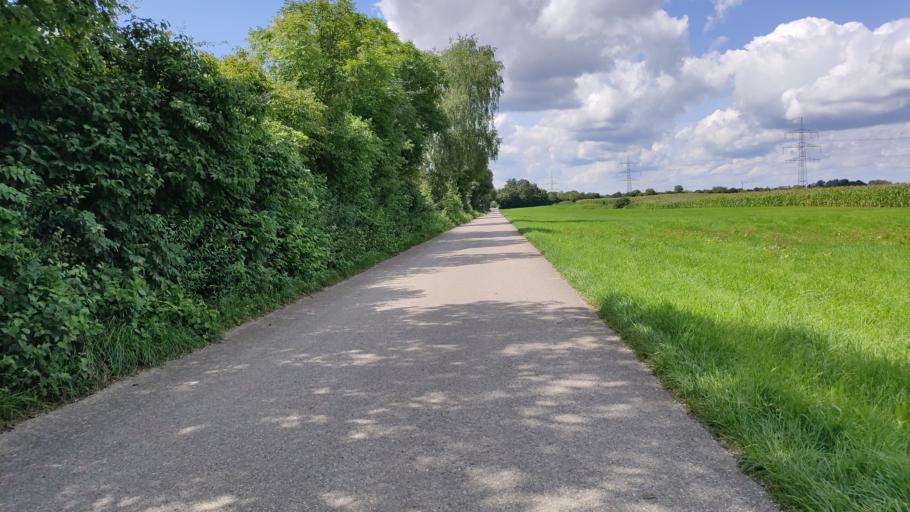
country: DE
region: Bavaria
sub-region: Swabia
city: Oberottmarshausen
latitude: 48.2309
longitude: 10.8821
